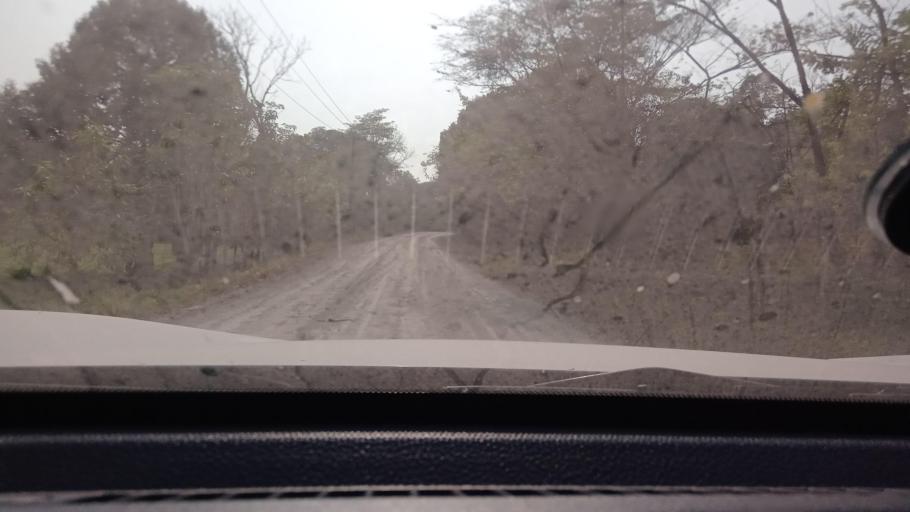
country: MX
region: Tabasco
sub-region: Huimanguillo
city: Francisco Rueda
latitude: 17.6205
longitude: -93.9497
